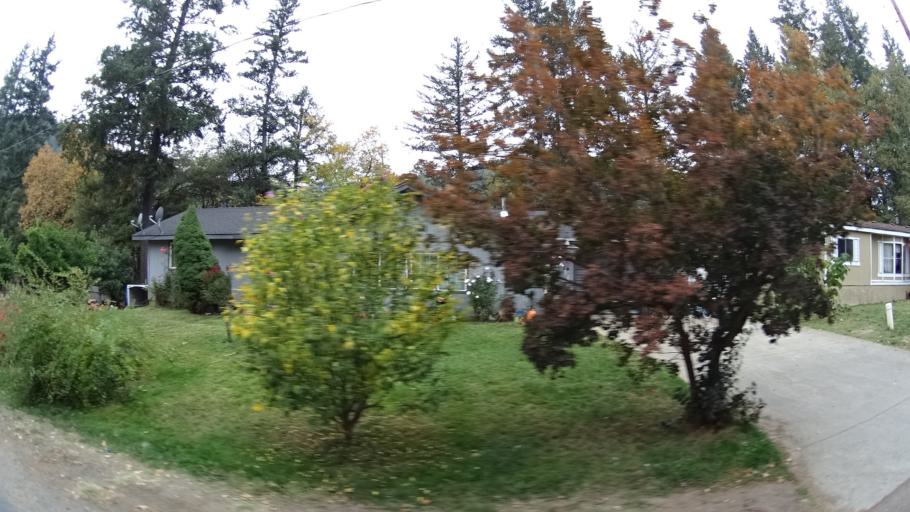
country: US
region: California
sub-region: Siskiyou County
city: Happy Camp
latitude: 41.8081
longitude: -123.3830
